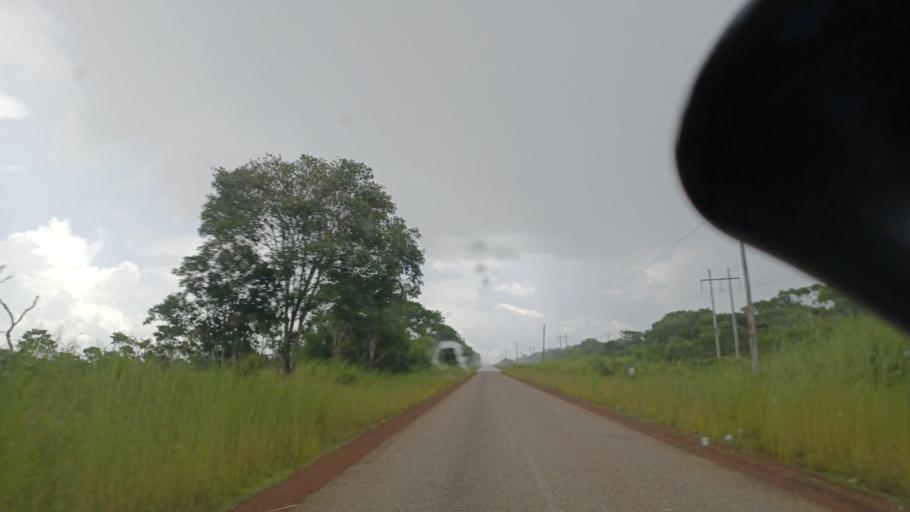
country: ZM
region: North-Western
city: Kasempa
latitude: -13.0927
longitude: 25.9228
